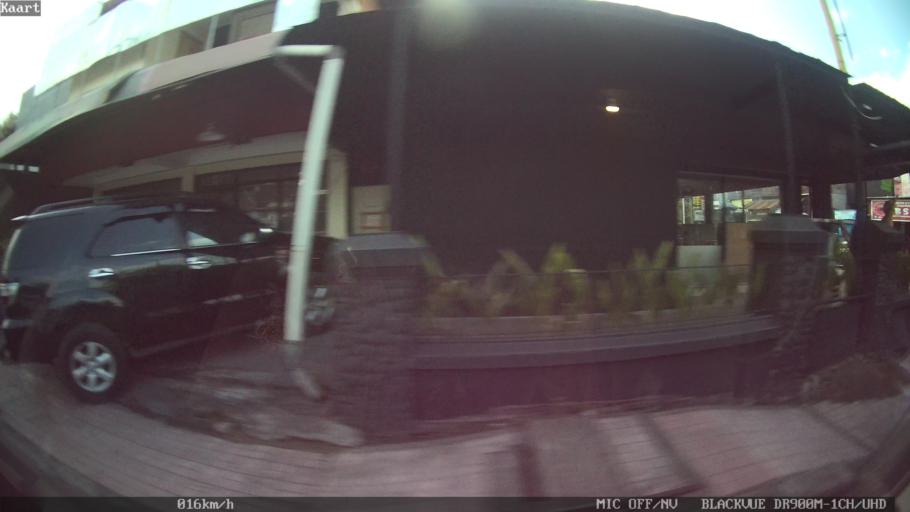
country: ID
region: Bali
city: Denpasar
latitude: -8.6771
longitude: 115.2101
